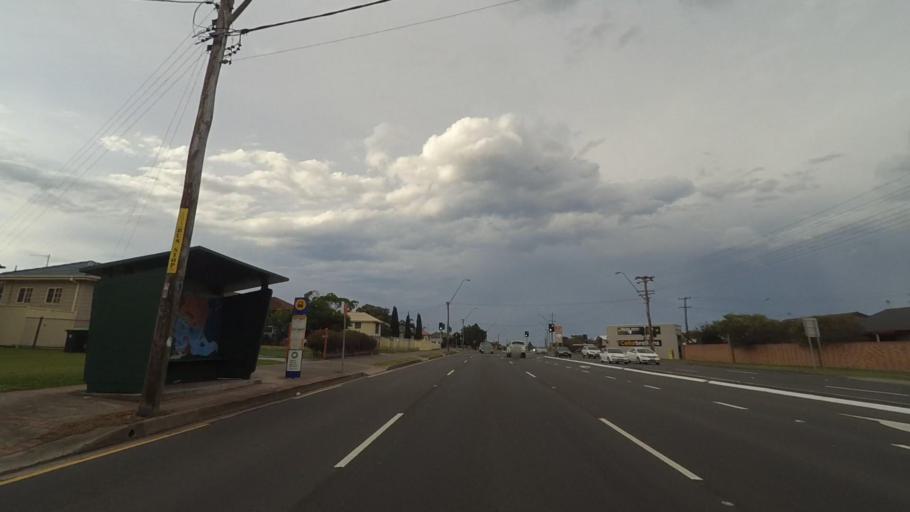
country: AU
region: New South Wales
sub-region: Shellharbour
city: Lake Illawarra
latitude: -34.5489
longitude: 150.8609
